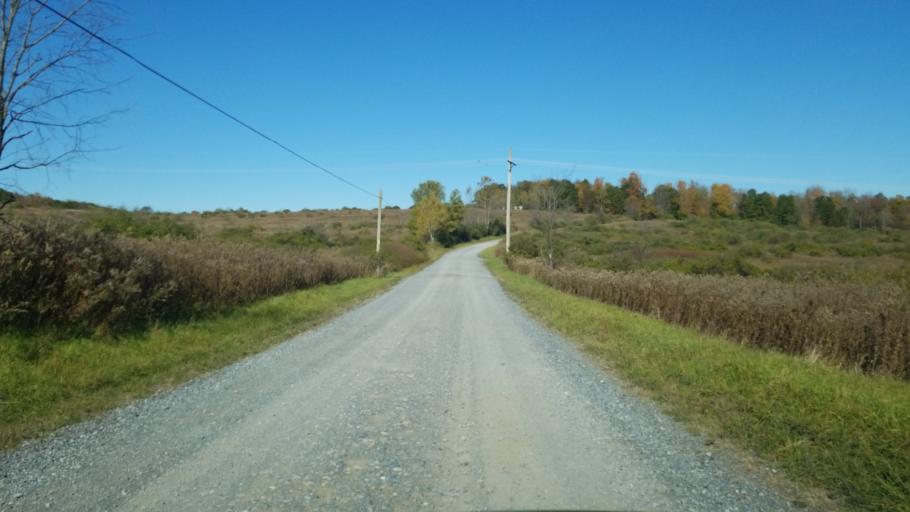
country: US
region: Pennsylvania
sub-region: Jefferson County
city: Falls Creek
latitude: 41.1839
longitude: -78.7831
